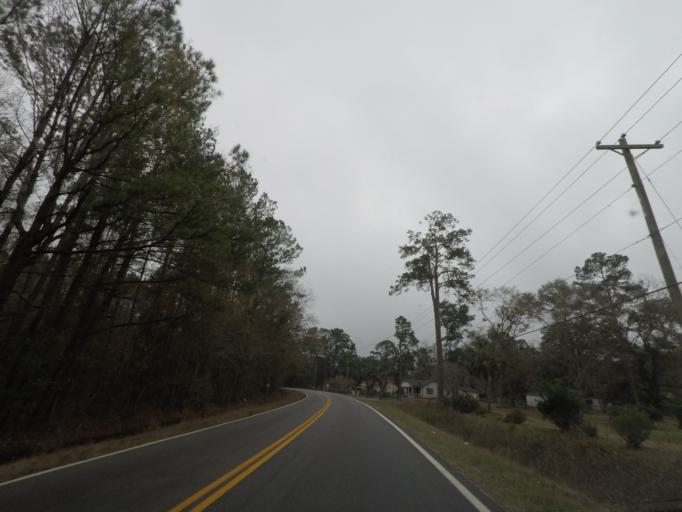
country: US
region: South Carolina
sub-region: Charleston County
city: Ravenel
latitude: 32.7254
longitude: -80.3533
